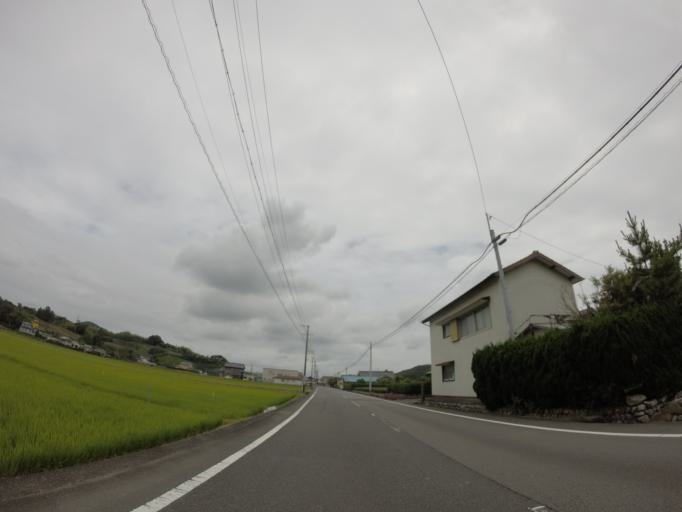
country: JP
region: Shizuoka
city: Shimada
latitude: 34.7697
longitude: 138.1829
